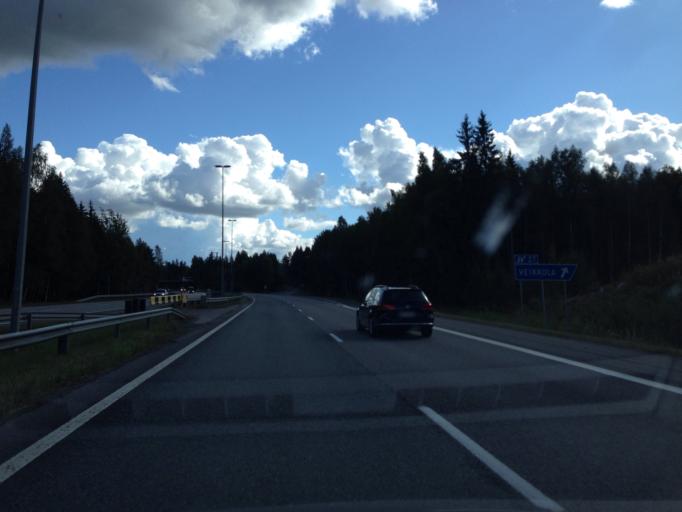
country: FI
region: Uusimaa
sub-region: Helsinki
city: Kirkkonummi
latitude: 60.2772
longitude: 24.4495
